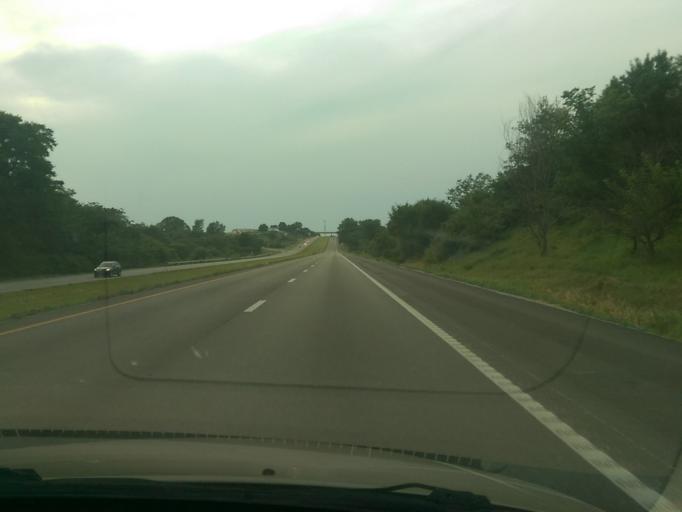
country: US
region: Missouri
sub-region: Andrew County
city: Savannah
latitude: 39.9095
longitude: -94.8939
